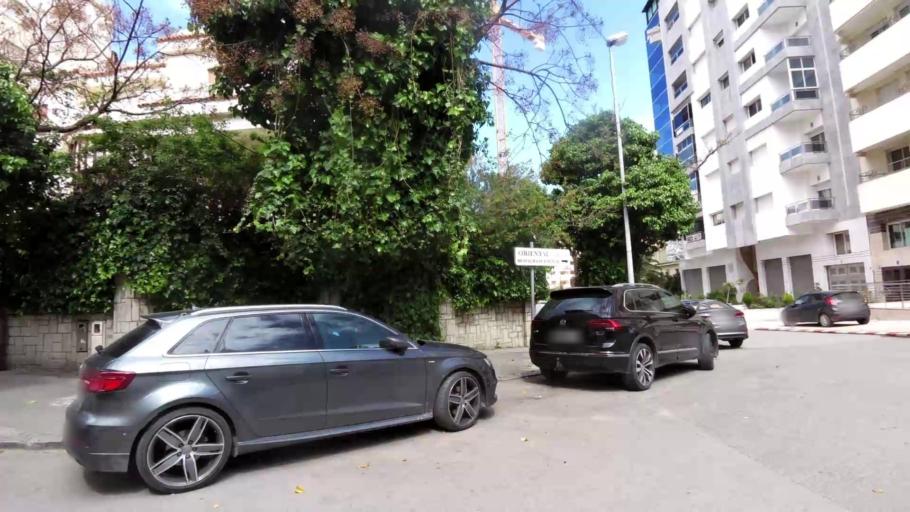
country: MA
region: Tanger-Tetouan
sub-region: Tanger-Assilah
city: Tangier
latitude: 35.7819
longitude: -5.8220
